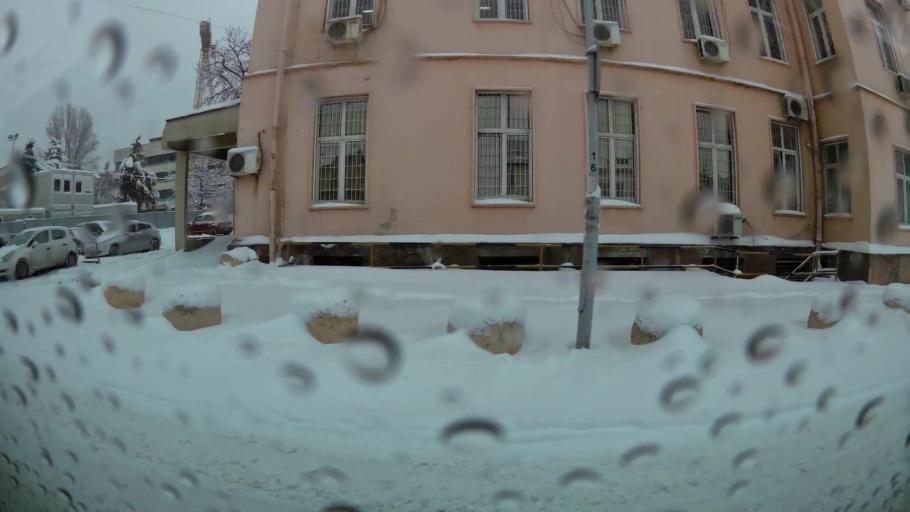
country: RS
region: Central Serbia
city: Belgrade
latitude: 44.7989
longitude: 20.4553
